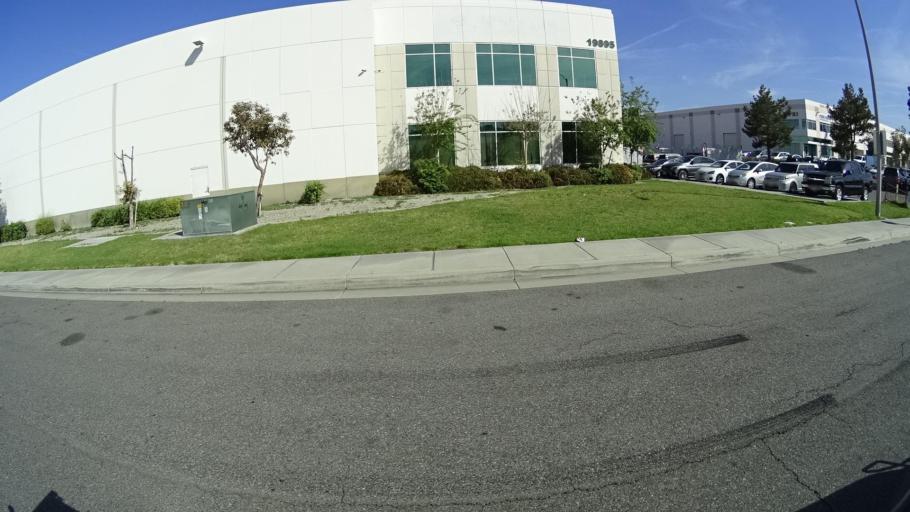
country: US
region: California
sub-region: Los Angeles County
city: Walnut
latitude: 34.0050
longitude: -117.8648
